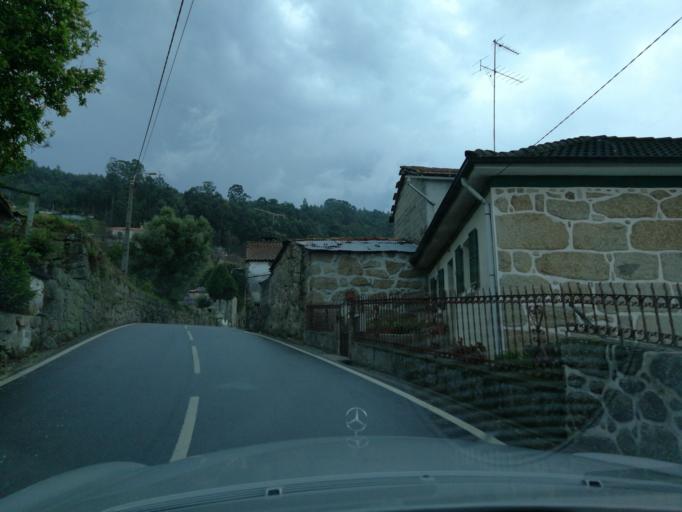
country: PT
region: Braga
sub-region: Braga
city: Oliveira
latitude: 41.4677
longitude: -8.4748
